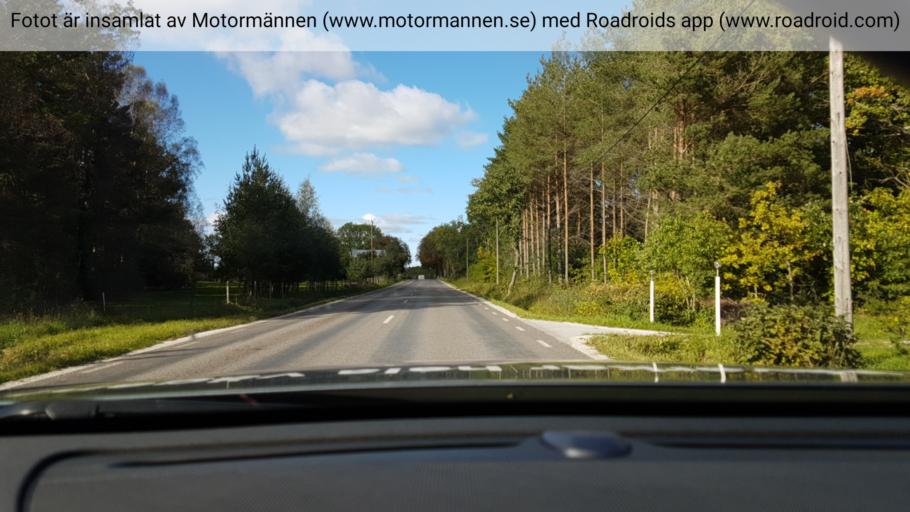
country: SE
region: Gotland
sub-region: Gotland
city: Klintehamn
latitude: 57.4463
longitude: 18.3668
